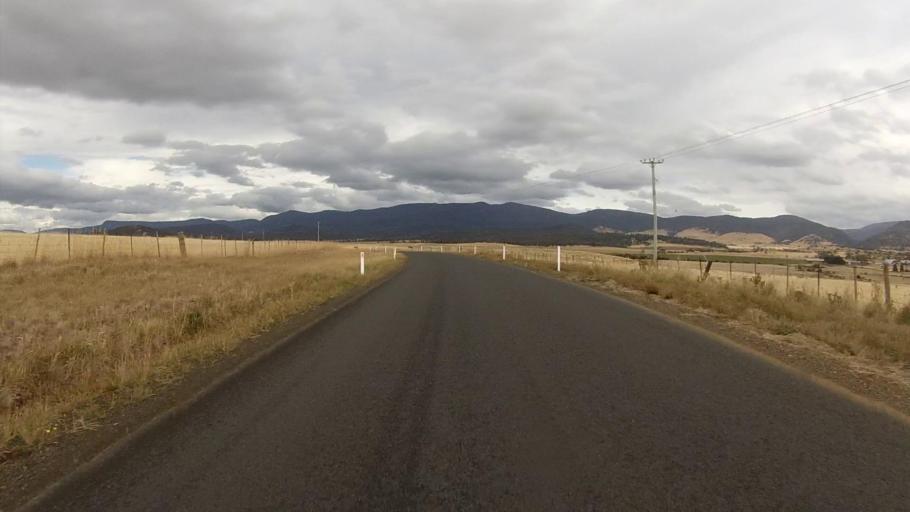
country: AU
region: Tasmania
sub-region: Northern Midlands
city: Evandale
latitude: -41.8225
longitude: 147.7591
